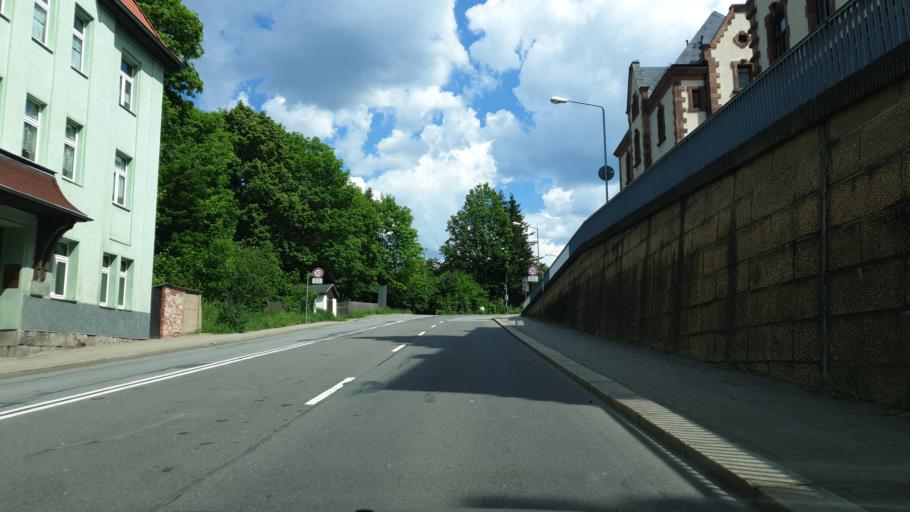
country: DE
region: Saxony
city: Aue
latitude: 50.5852
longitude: 12.7068
